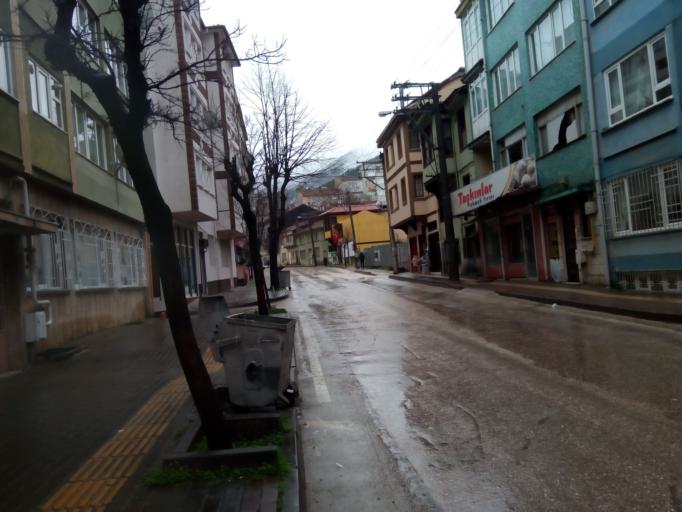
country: TR
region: Bursa
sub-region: Osmangazi
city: Bursa
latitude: 40.1779
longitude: 29.0606
